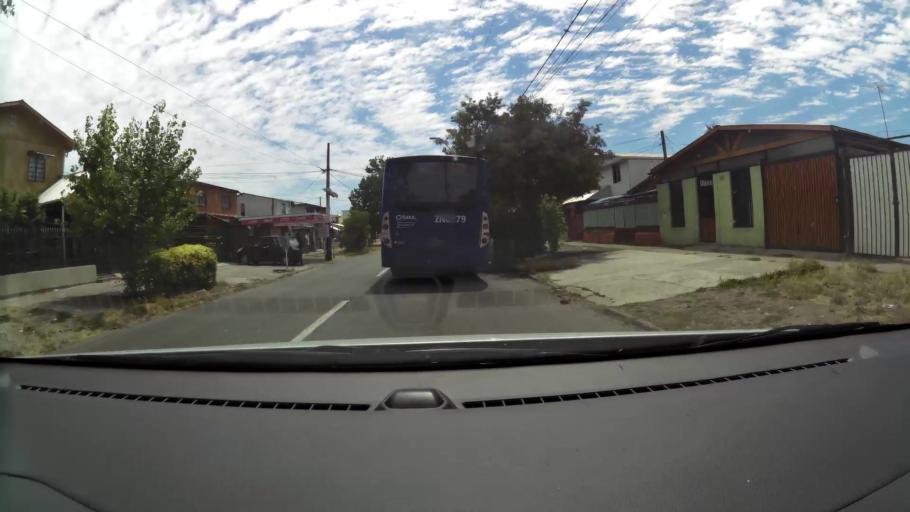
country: CL
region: Santiago Metropolitan
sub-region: Provincia de Santiago
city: La Pintana
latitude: -33.5835
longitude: -70.6543
